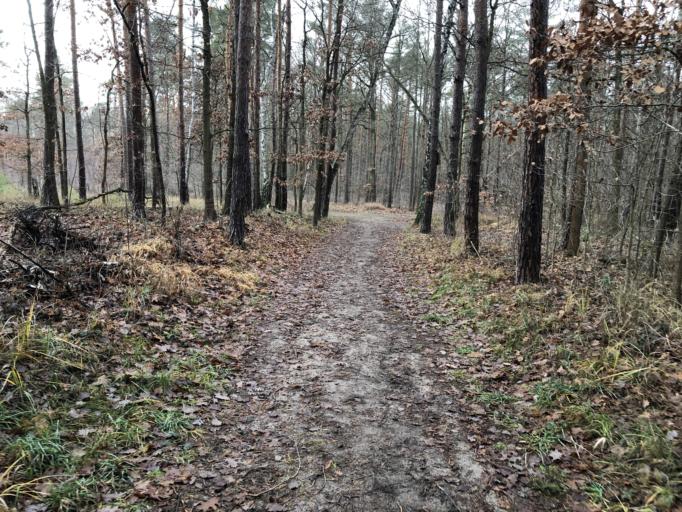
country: DE
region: Saxony-Anhalt
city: Halle Neustadt
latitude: 51.5001
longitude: 11.8940
